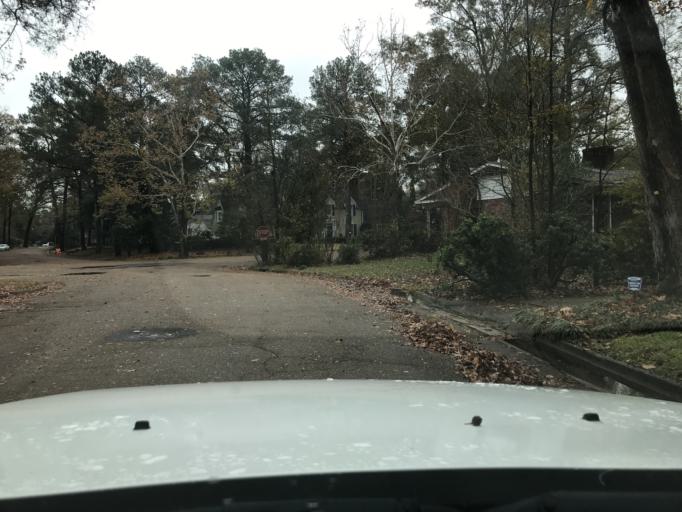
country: US
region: Mississippi
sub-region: Rankin County
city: Flowood
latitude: 32.3420
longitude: -90.1700
